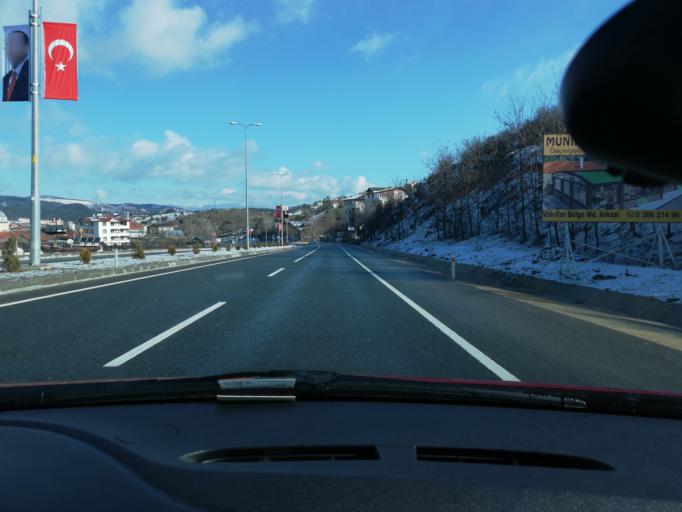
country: TR
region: Kastamonu
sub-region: Cide
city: Kastamonu
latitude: 41.3423
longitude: 33.7666
